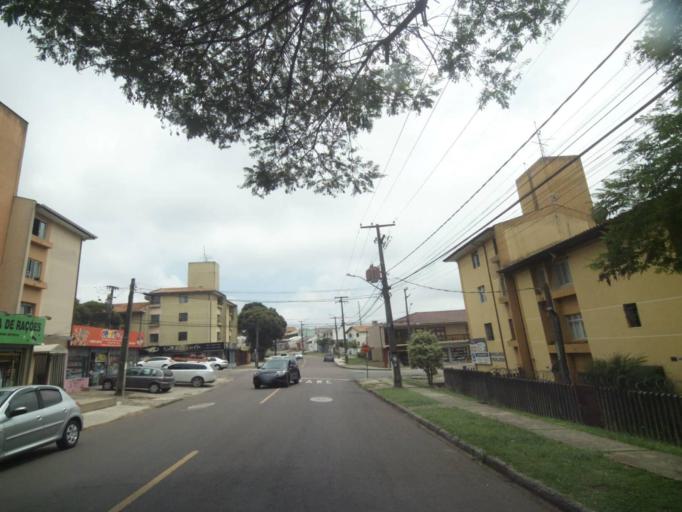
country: BR
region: Parana
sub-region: Curitiba
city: Curitiba
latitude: -25.4851
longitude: -49.3520
